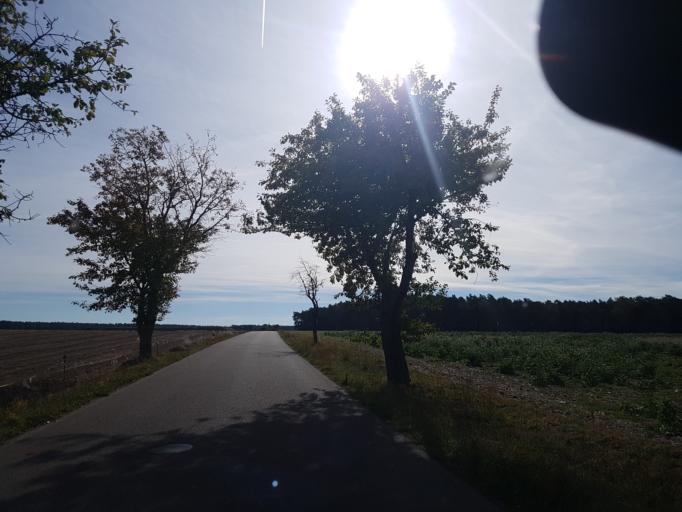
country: DE
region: Brandenburg
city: Schlieben
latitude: 51.7753
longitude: 13.3271
